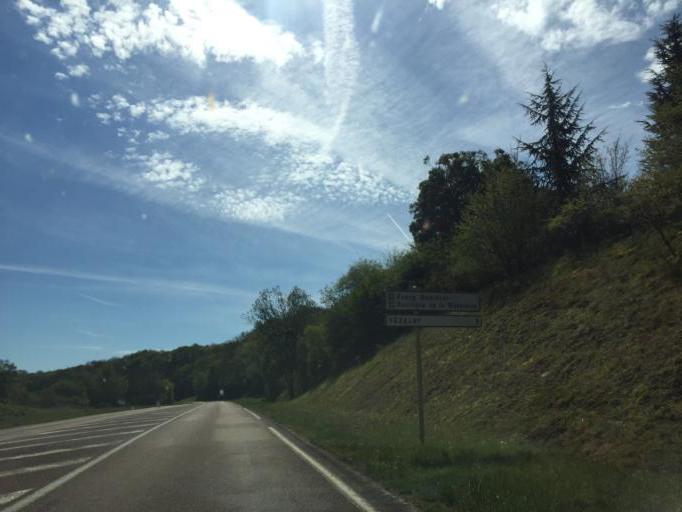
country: FR
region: Bourgogne
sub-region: Departement de la Nievre
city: Clamecy
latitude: 47.4565
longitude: 3.6514
